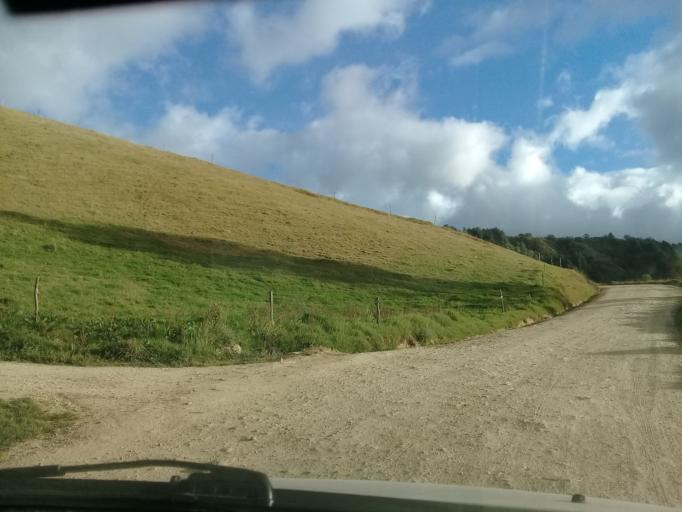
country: CO
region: Cundinamarca
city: Villapinzon
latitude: 5.2138
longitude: -73.6306
